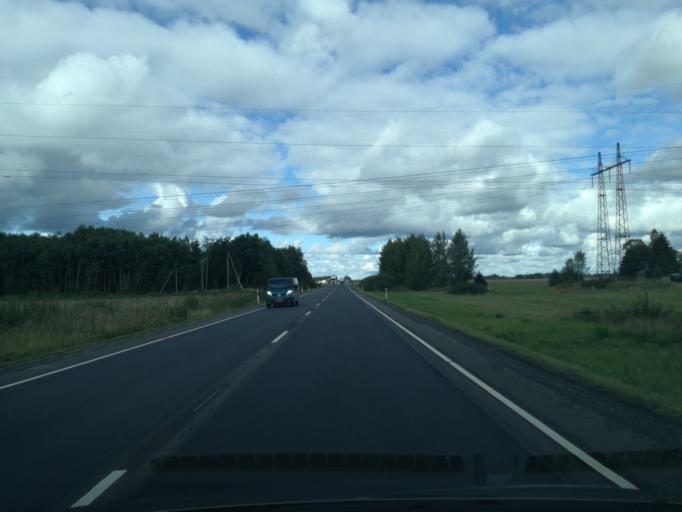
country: EE
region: Harju
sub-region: Saku vald
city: Saku
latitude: 59.2614
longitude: 24.7410
